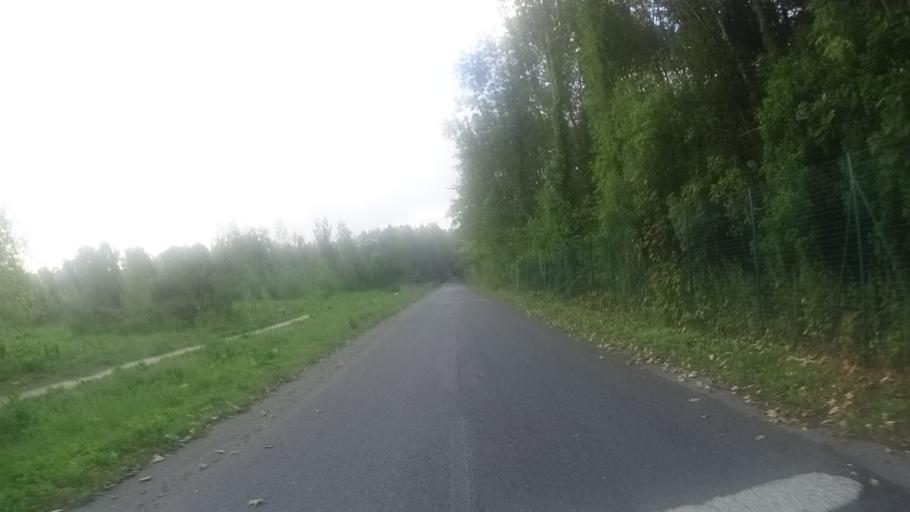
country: FR
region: Ile-de-France
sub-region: Departement de l'Essonne
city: Mennecy
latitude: 48.5690
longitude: 2.4132
